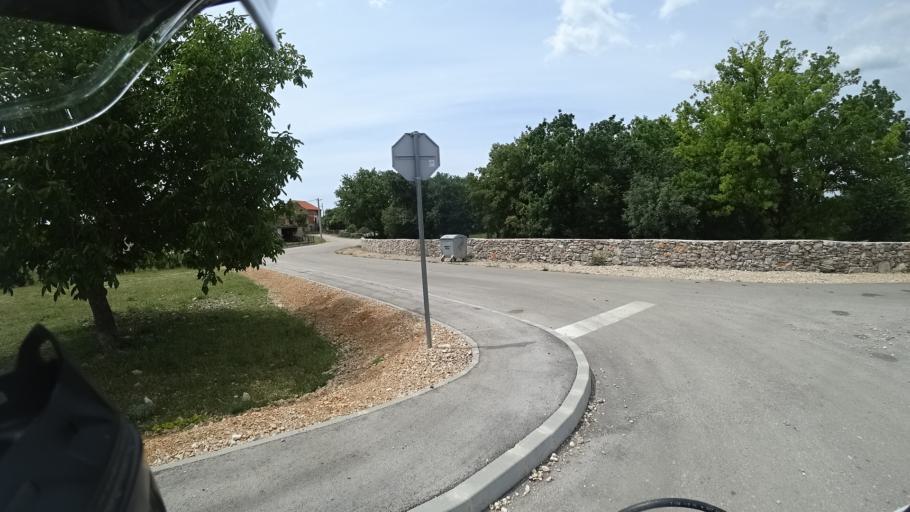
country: HR
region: Sibensko-Kniniska
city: Kistanje
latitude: 44.0853
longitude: 15.9592
